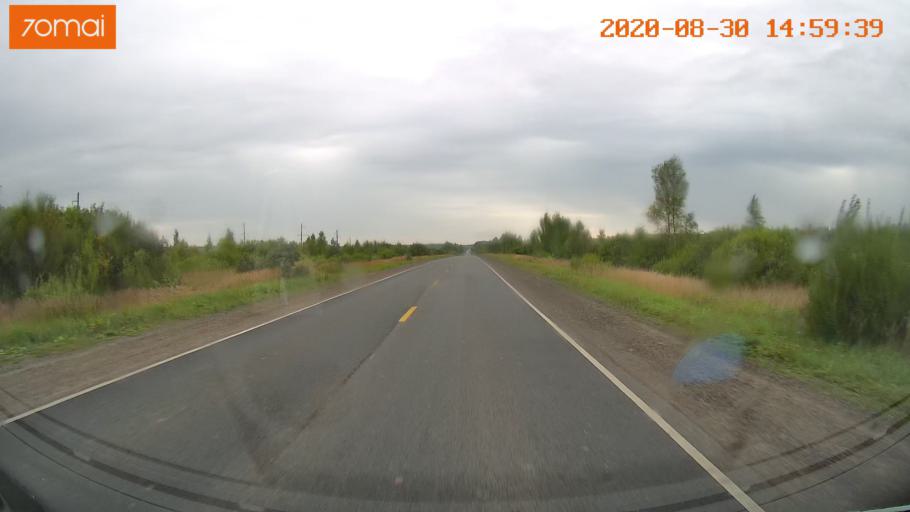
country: RU
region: Ivanovo
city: Staraya Vichuga
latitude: 57.3394
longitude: 41.9700
